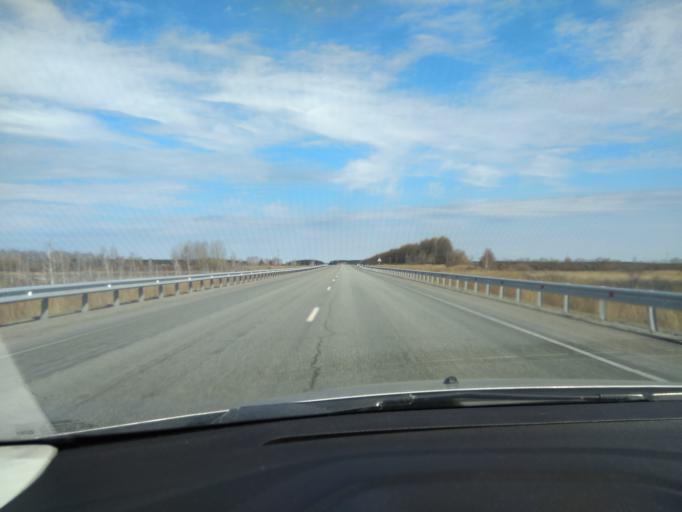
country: RU
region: Sverdlovsk
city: Troitskiy
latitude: 57.0861
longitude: 63.7092
